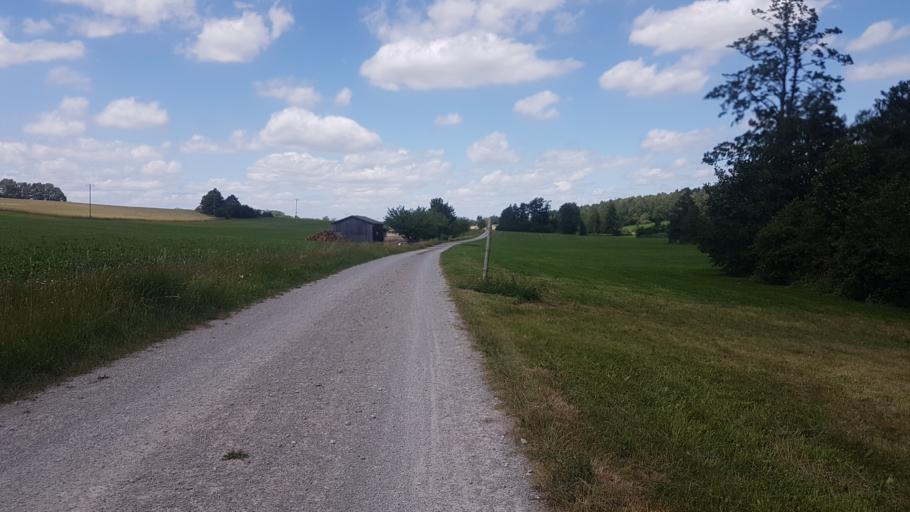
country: DE
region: Bavaria
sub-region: Regierungsbezirk Mittelfranken
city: Leutershausen
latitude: 49.3162
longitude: 10.3874
